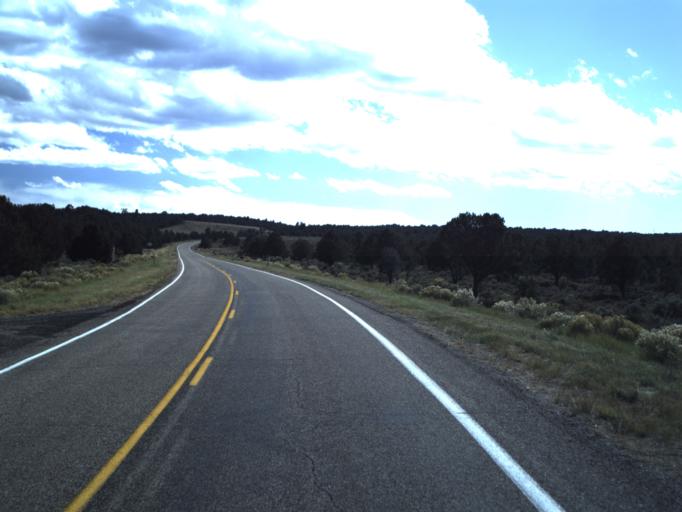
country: US
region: Utah
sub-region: Garfield County
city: Panguitch
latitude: 37.7891
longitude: -112.4394
